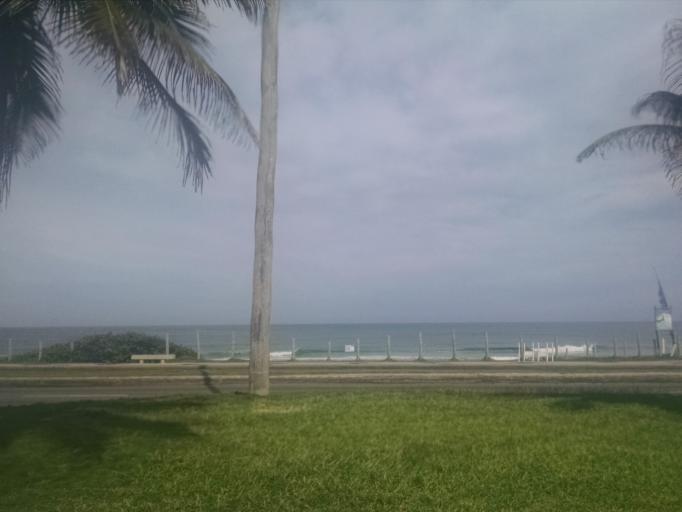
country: BR
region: Rio de Janeiro
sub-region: Rio De Janeiro
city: Rio de Janeiro
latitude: -23.0102
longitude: -43.3470
